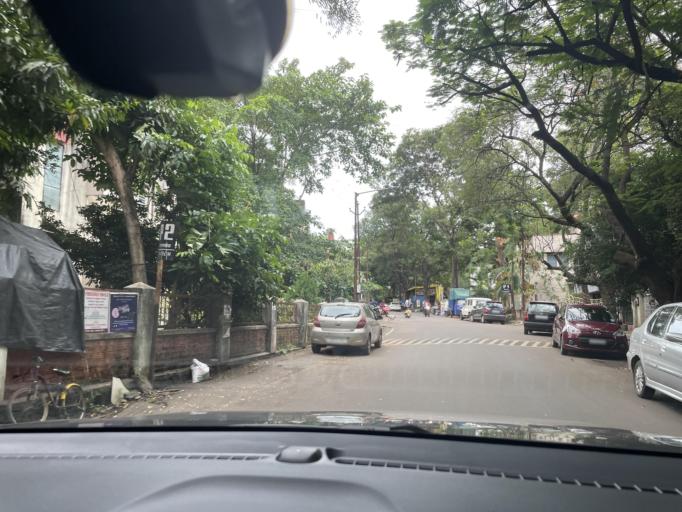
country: IN
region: Maharashtra
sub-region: Pune Division
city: Shivaji Nagar
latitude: 18.5313
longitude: 73.8111
